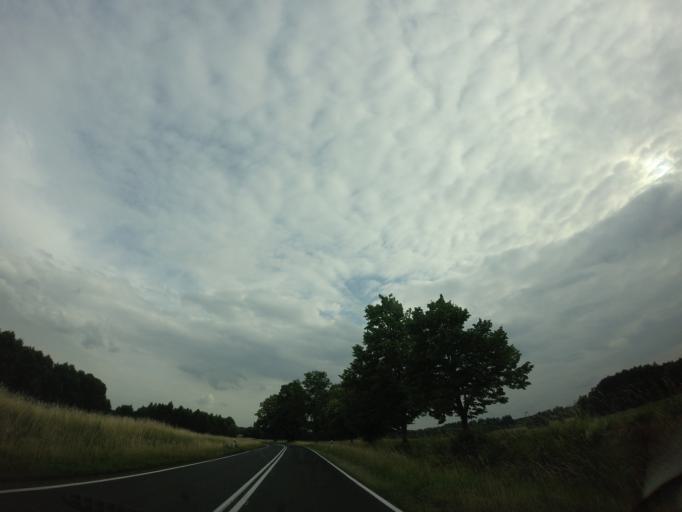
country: PL
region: West Pomeranian Voivodeship
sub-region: Powiat szczecinecki
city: Borne Sulinowo
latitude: 53.6476
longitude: 16.6112
